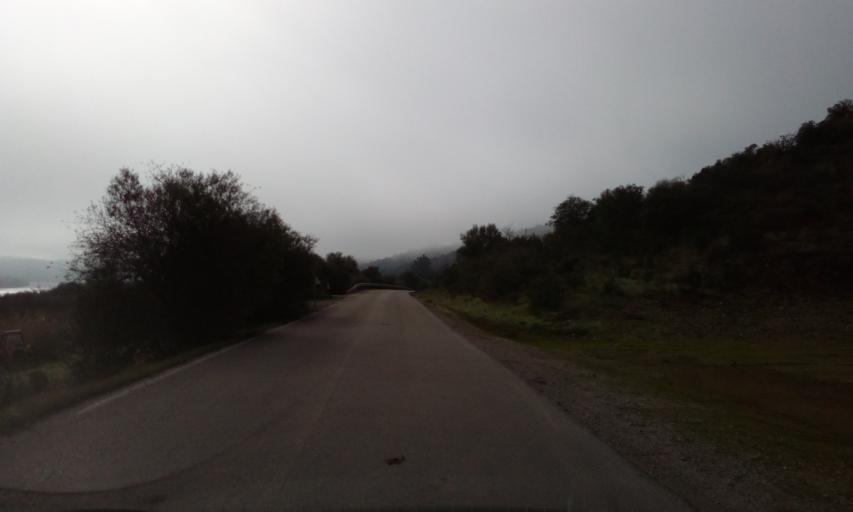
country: ES
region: Andalusia
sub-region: Provincia de Huelva
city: Sanlucar de Guadiana
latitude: 37.4432
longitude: -7.4610
